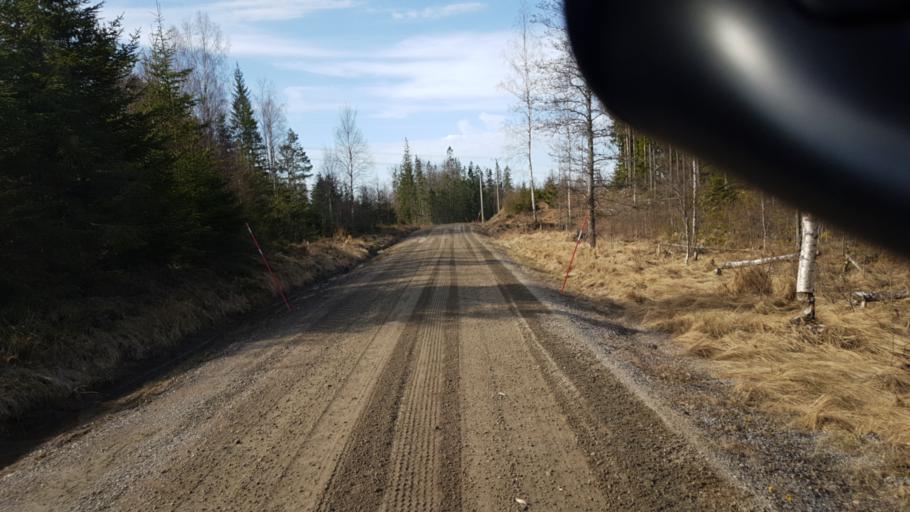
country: SE
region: Vaermland
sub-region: Arvika Kommun
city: Arvika
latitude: 59.5391
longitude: 12.4199
